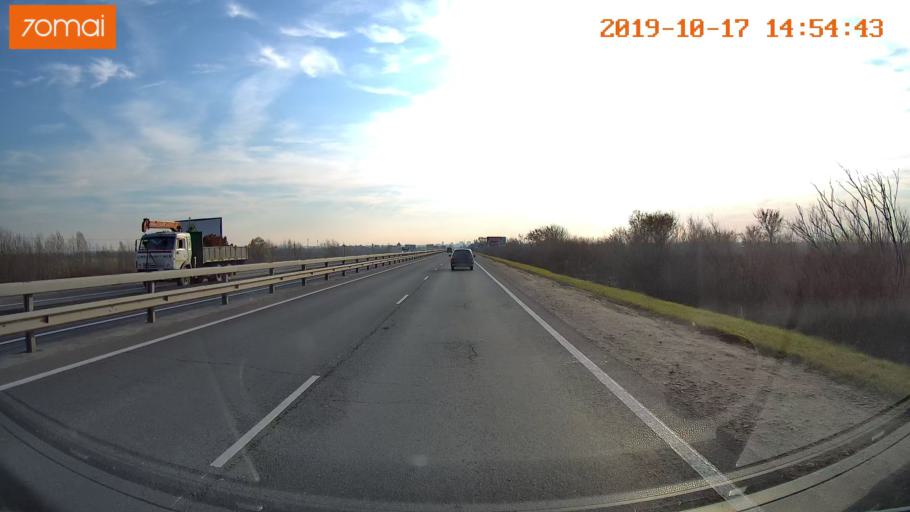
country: RU
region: Rjazan
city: Polyany
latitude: 54.6780
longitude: 39.8299
